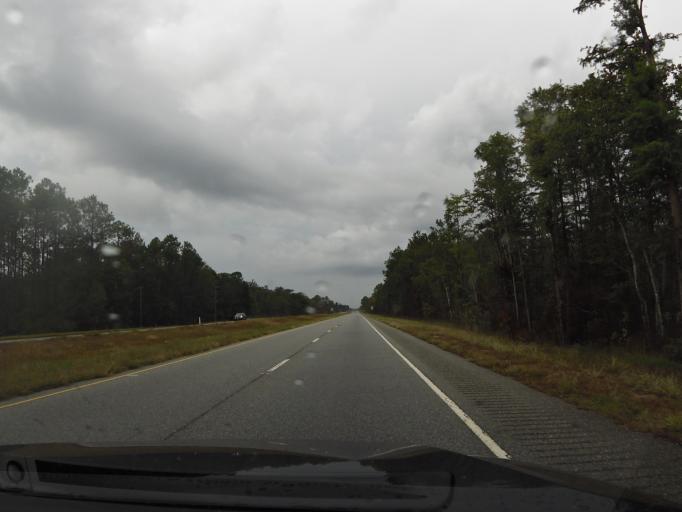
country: US
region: Georgia
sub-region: Wayne County
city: Jesup
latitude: 31.5261
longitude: -81.7845
